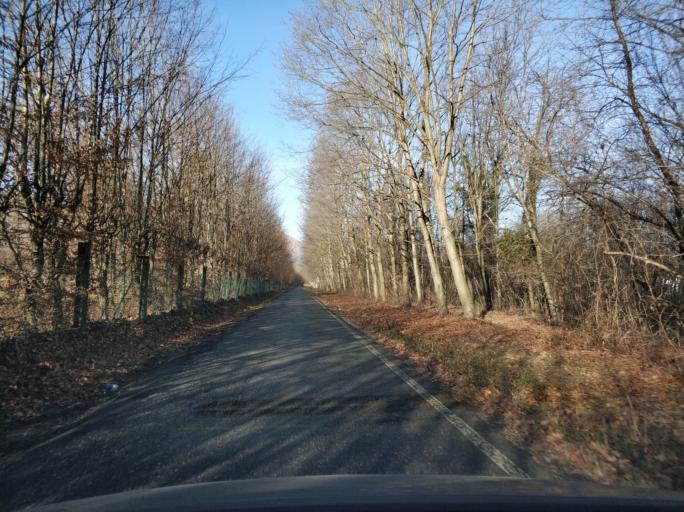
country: IT
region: Piedmont
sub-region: Provincia di Torino
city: Fiano
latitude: 45.2178
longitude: 7.5453
